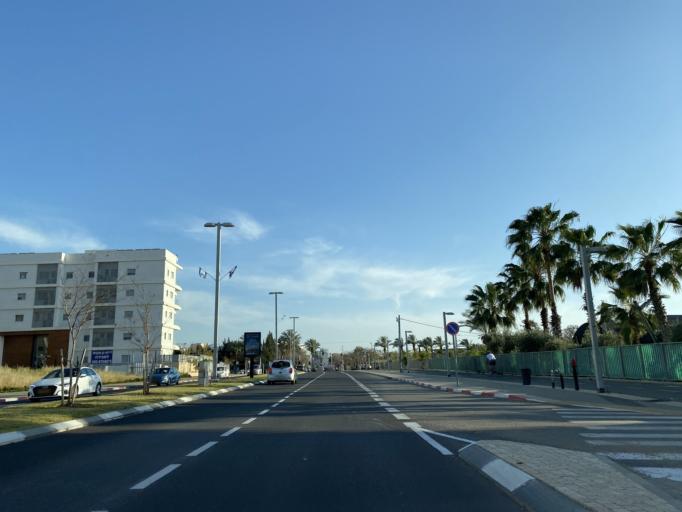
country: IL
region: Tel Aviv
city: Herzliyya
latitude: 32.1729
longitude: 34.8292
